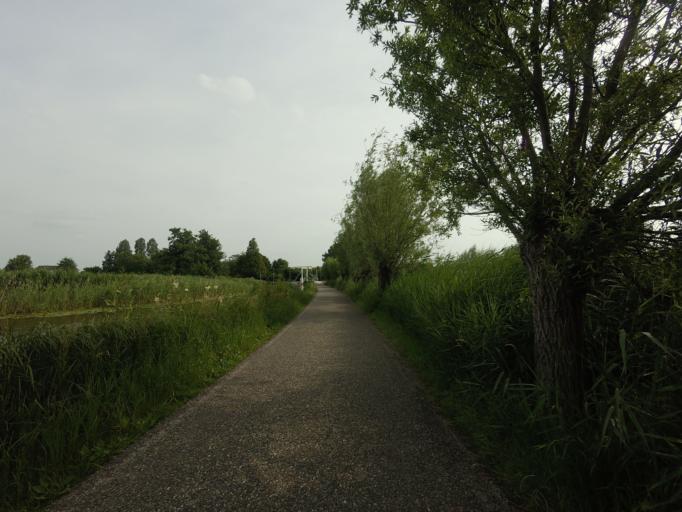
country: NL
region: South Holland
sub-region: Bodegraven-Reeuwijk
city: Reeuwijk
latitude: 52.0362
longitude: 4.7555
